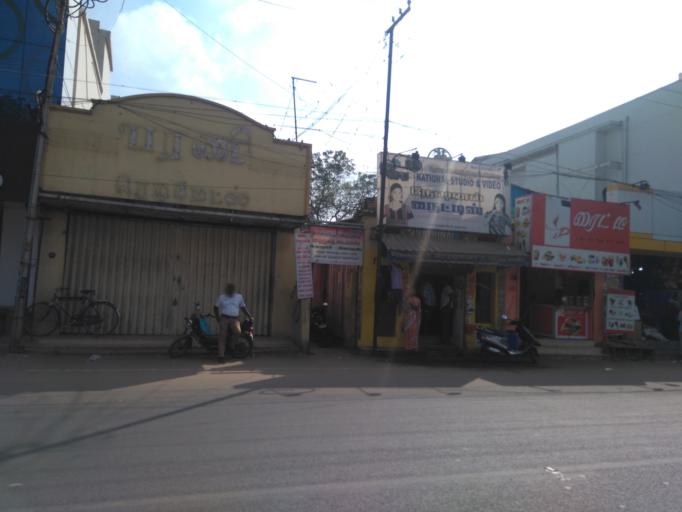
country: IN
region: Tamil Nadu
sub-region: Thanjavur
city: Thanjavur
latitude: 10.7849
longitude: 79.1389
